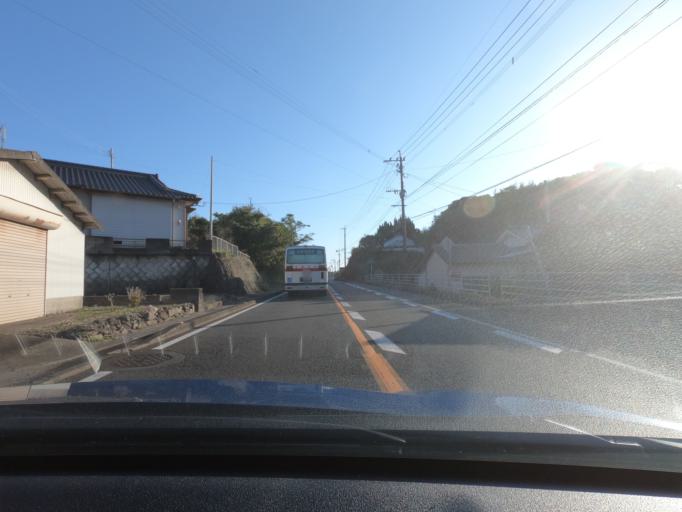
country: JP
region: Kagoshima
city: Akune
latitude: 31.9855
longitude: 130.2039
